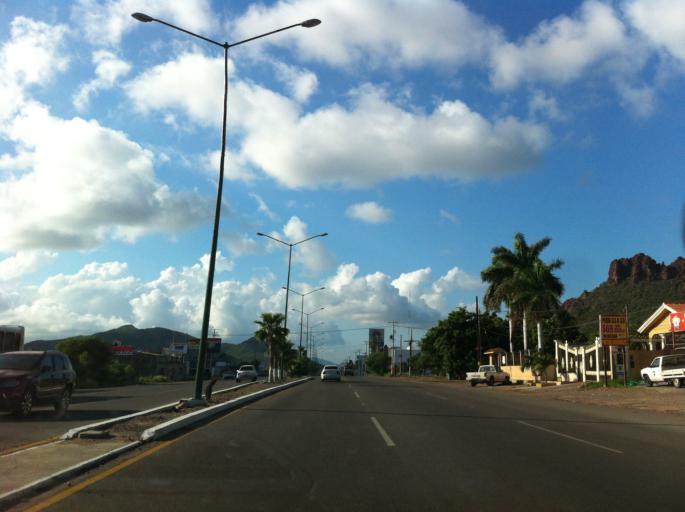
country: MX
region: Sonora
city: Heroica Guaymas
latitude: 27.9315
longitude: -110.9254
